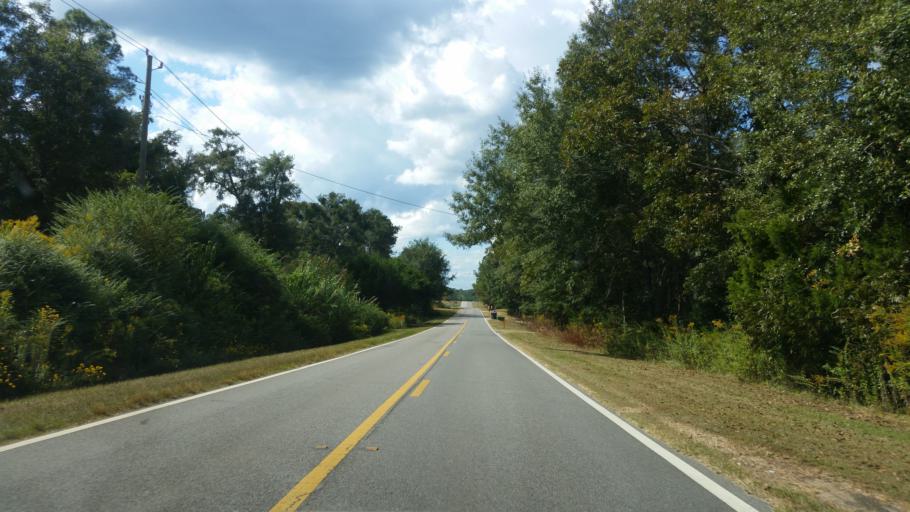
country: US
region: Alabama
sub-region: Escambia County
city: Atmore
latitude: 30.8855
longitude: -87.5104
